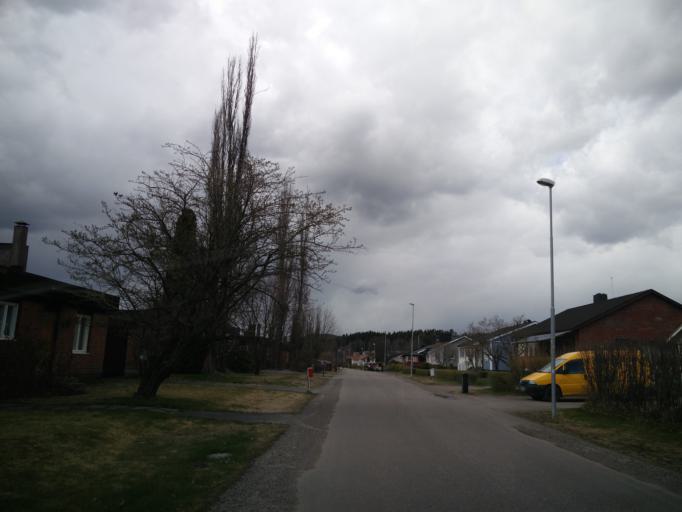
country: SE
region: Vaesternorrland
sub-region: Sundsvalls Kommun
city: Sundsvall
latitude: 62.4014
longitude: 17.2624
